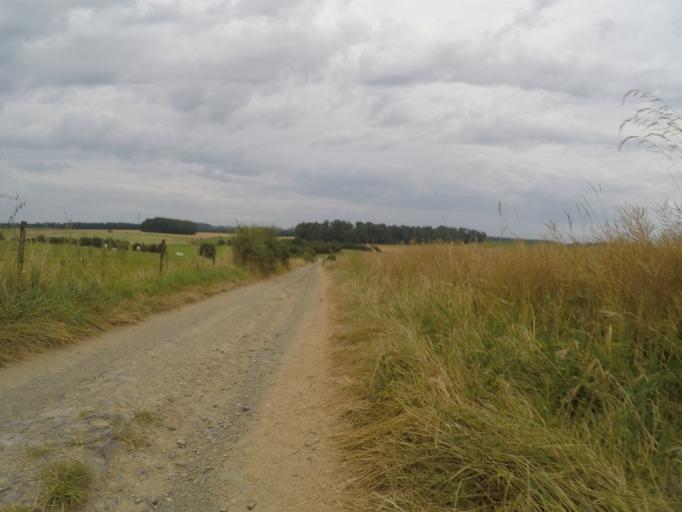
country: BE
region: Wallonia
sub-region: Province de Namur
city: Assesse
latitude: 50.3034
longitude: 5.0011
